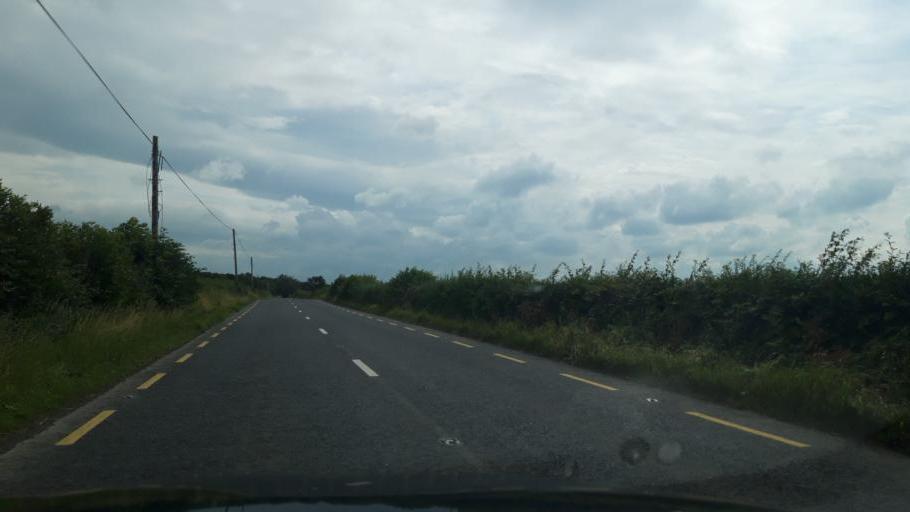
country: IE
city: Ballylinan
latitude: 52.9699
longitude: -7.0177
